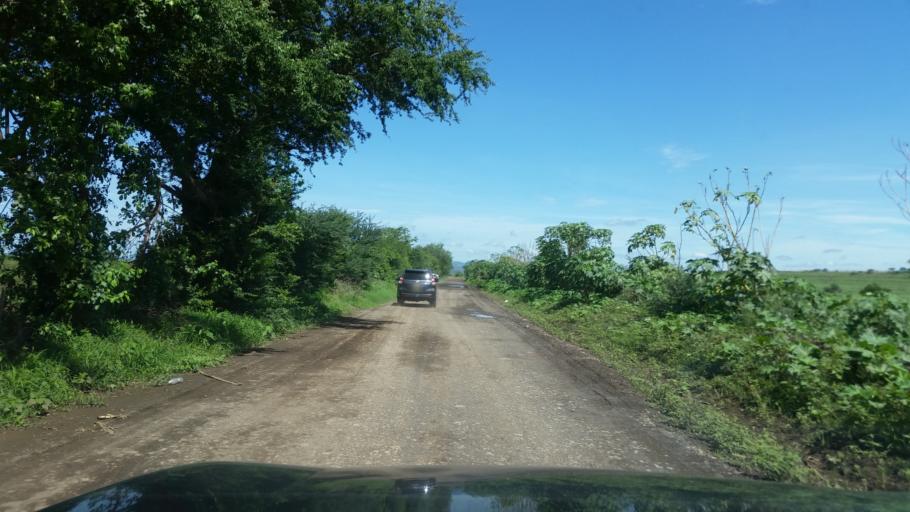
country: NI
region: Chinandega
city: Puerto Morazan
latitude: 12.7728
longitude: -87.0965
